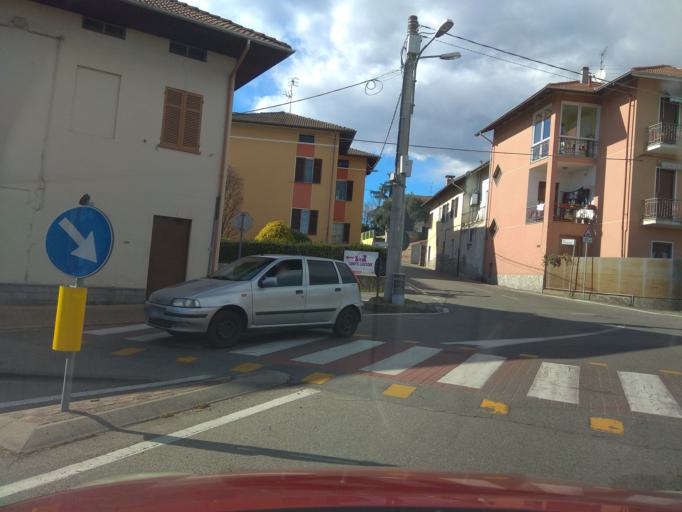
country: IT
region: Piedmont
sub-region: Provincia di Biella
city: Cossato
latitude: 45.5757
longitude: 8.1800
